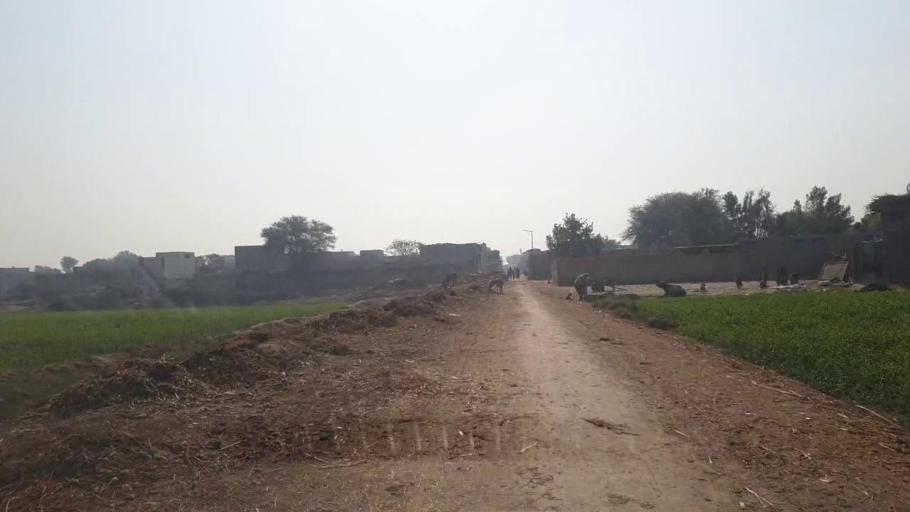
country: PK
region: Sindh
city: Tando Allahyar
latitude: 25.3638
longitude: 68.6485
